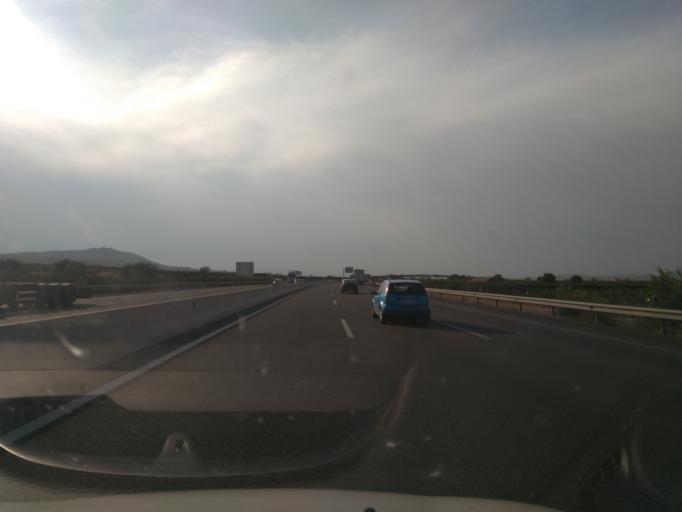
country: ES
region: Valencia
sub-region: Provincia de Valencia
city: Torrent
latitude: 39.4237
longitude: -0.5203
